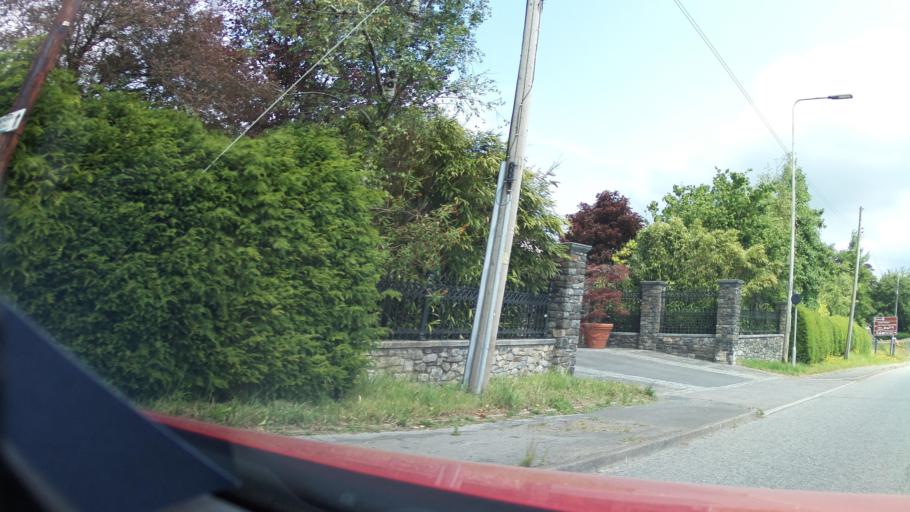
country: GB
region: Wales
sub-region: Vale of Glamorgan
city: Rhoose
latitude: 51.4580
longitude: -3.3408
